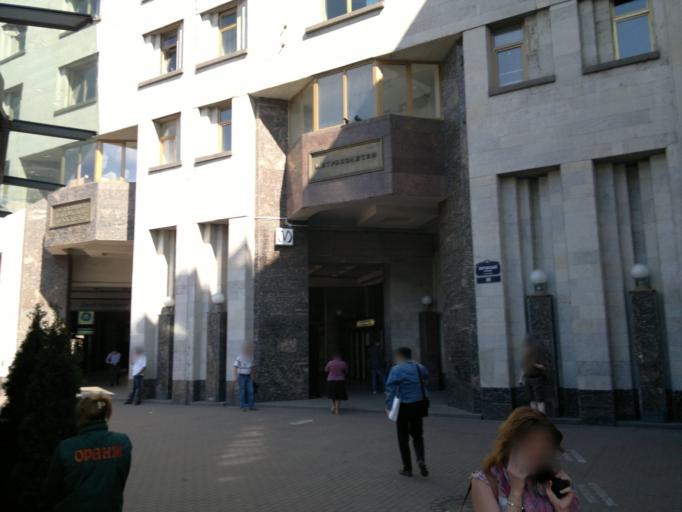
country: RU
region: St.-Petersburg
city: Centralniy
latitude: 59.9207
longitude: 30.3545
